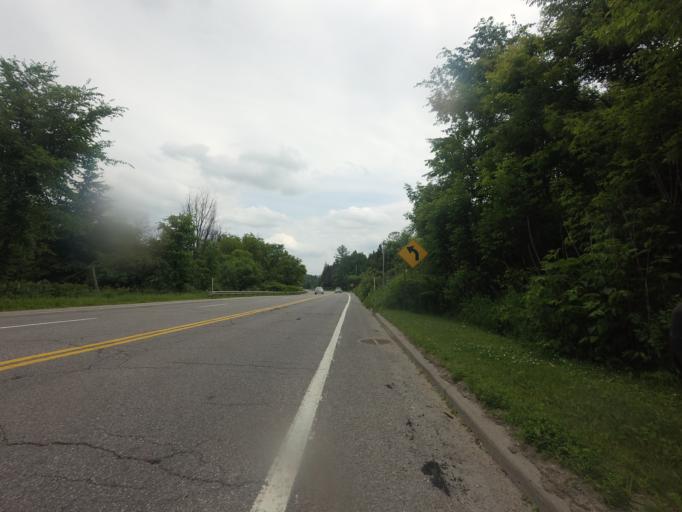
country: CA
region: Quebec
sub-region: Outaouais
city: Wakefield
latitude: 45.7454
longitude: -75.9113
